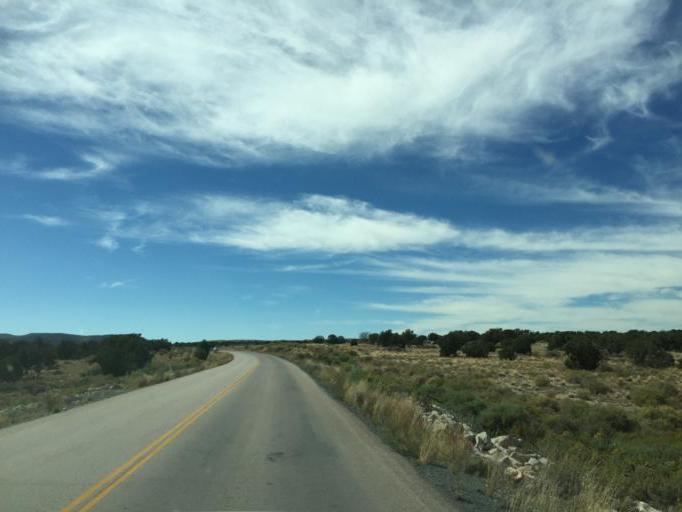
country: US
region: Arizona
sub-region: Mohave County
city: Meadview
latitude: 35.9600
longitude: -113.8353
